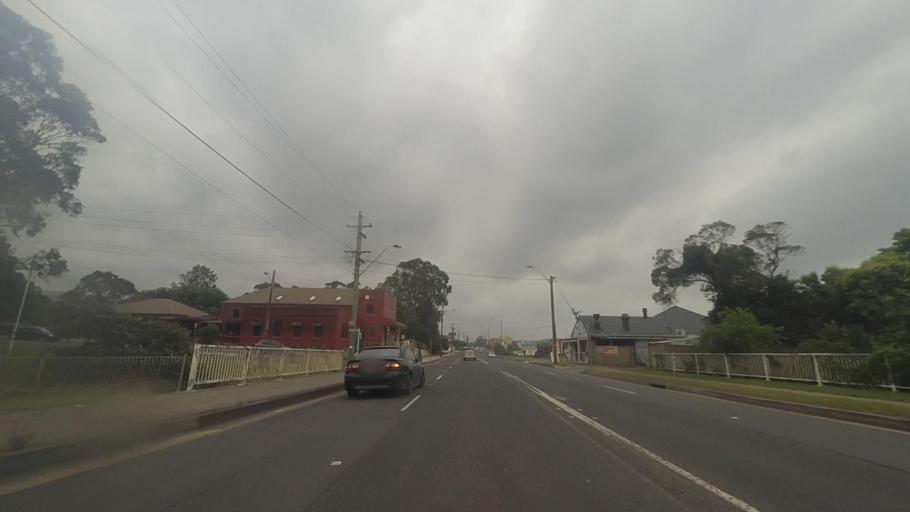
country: AU
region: New South Wales
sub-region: Wollongong
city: Cordeaux Heights
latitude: -34.4578
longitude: 150.8421
